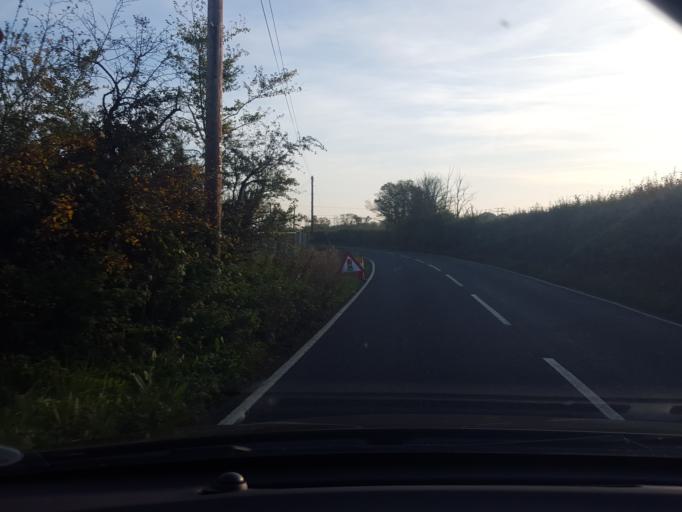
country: GB
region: England
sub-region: Essex
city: Little Clacton
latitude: 51.8235
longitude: 1.1613
